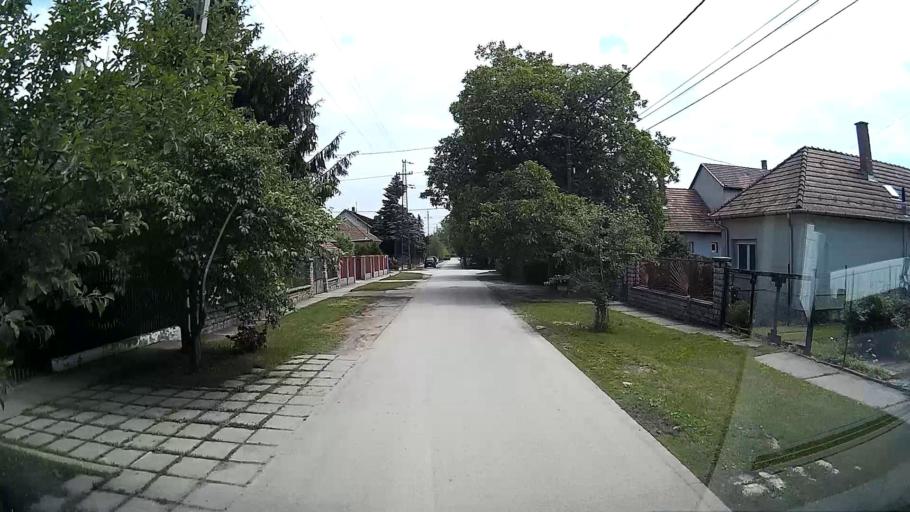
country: HU
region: Pest
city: Pomaz
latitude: 47.6451
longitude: 19.0364
